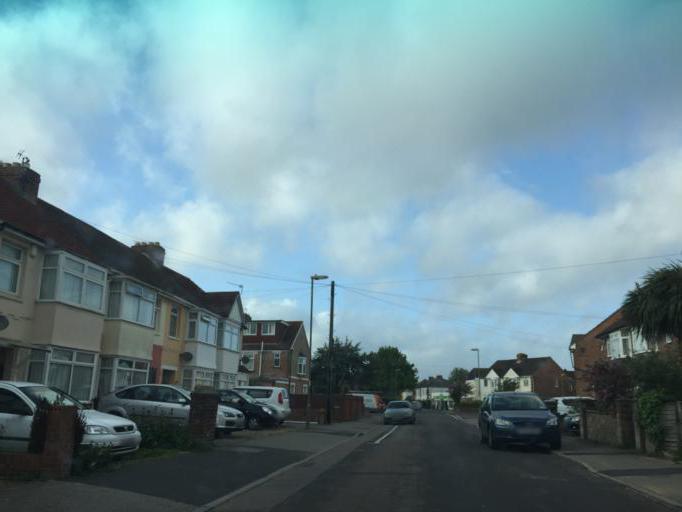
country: GB
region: England
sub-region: Hampshire
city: Gosport
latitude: 50.8072
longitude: -1.1460
